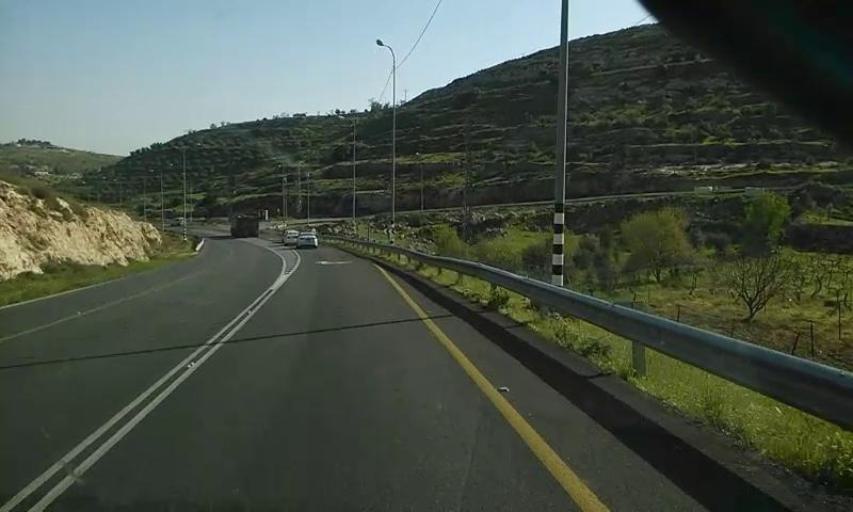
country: PS
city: Al Buq`ah
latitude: 31.5187
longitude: 35.1325
